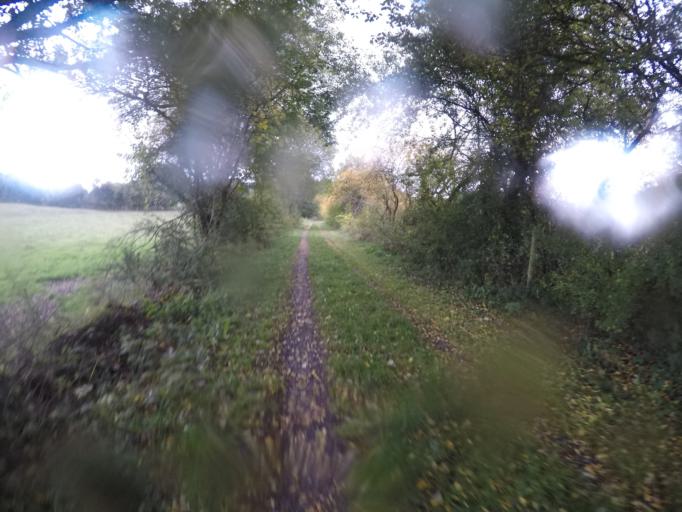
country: BE
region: Wallonia
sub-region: Province du Luxembourg
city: Fauvillers
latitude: 49.8754
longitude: 5.6807
